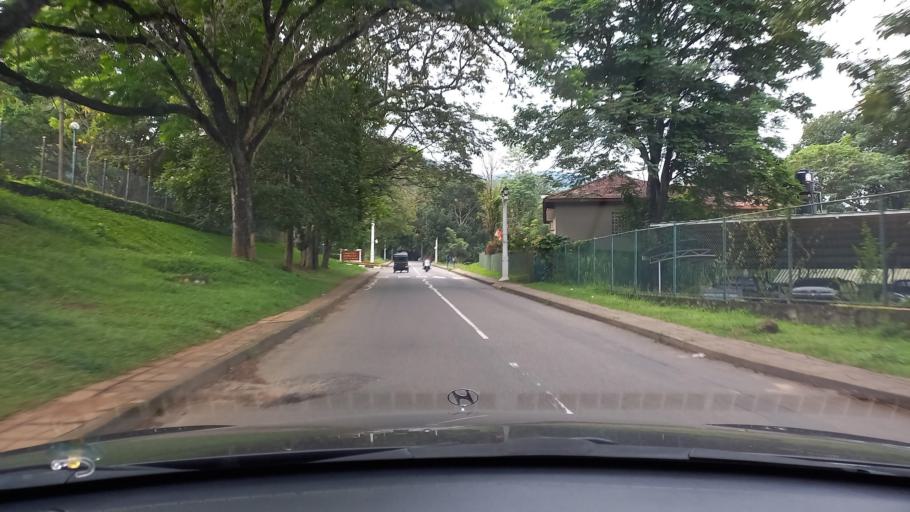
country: LK
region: Central
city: Kandy
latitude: 7.2635
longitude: 80.5978
